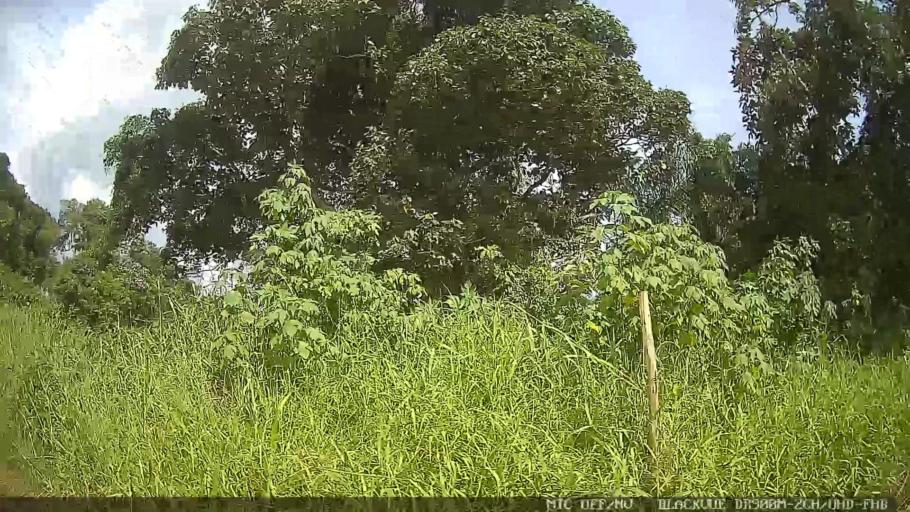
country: BR
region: Sao Paulo
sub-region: Mogi das Cruzes
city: Mogi das Cruzes
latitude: -23.6349
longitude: -46.2115
